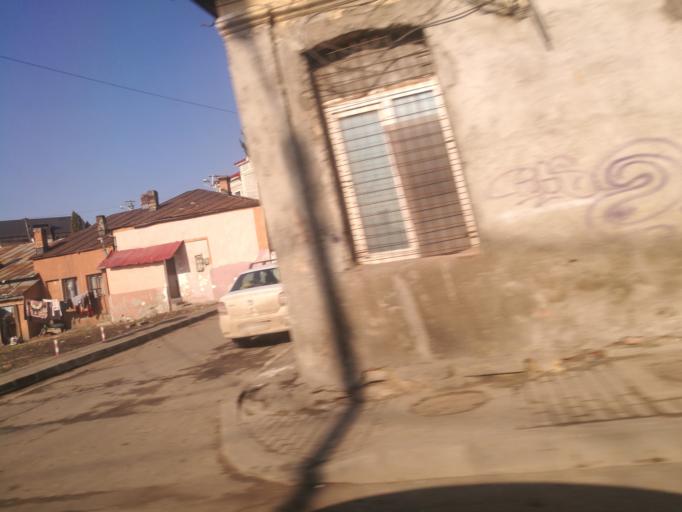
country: RO
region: Iasi
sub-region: Municipiul Iasi
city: Iasi
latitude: 47.1726
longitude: 27.5652
